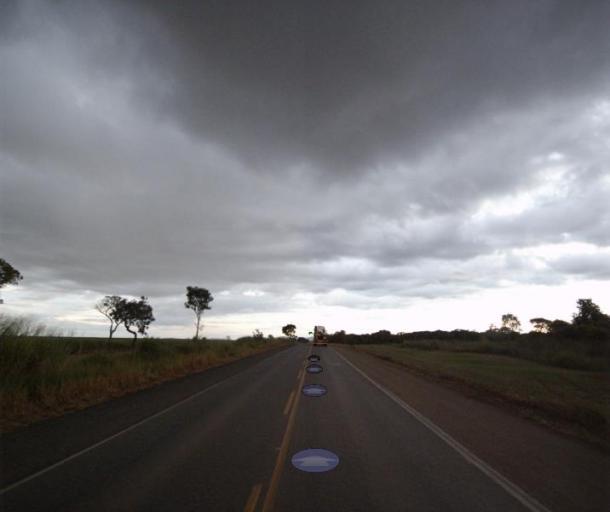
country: BR
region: Goias
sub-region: Uruacu
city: Uruacu
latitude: -14.6539
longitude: -49.1885
